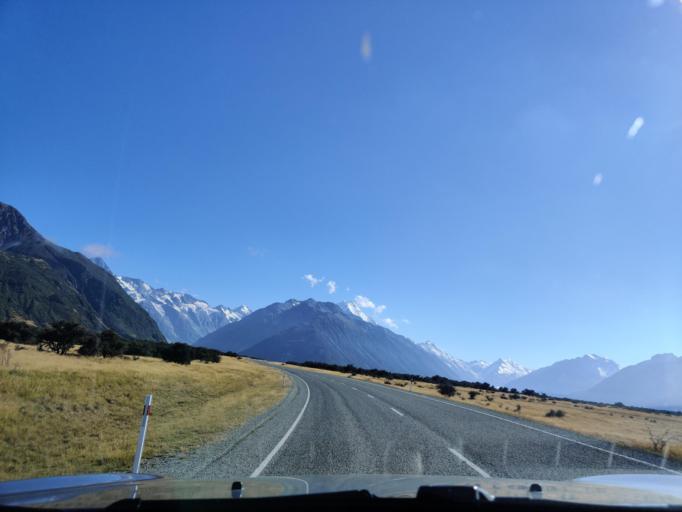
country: NZ
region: Canterbury
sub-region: Timaru District
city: Pleasant Point
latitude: -43.7818
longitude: 170.1236
